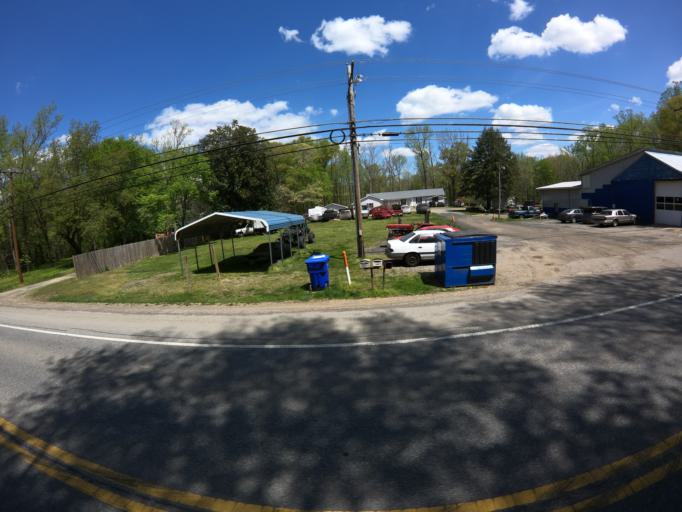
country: US
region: Maryland
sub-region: Charles County
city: Potomac Heights
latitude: 38.5813
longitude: -77.1162
